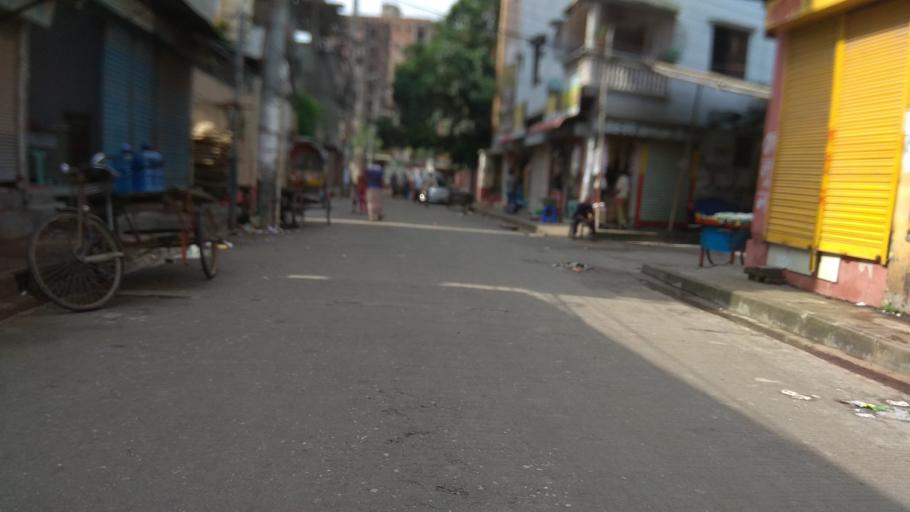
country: BD
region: Dhaka
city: Azimpur
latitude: 23.7997
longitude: 90.3563
